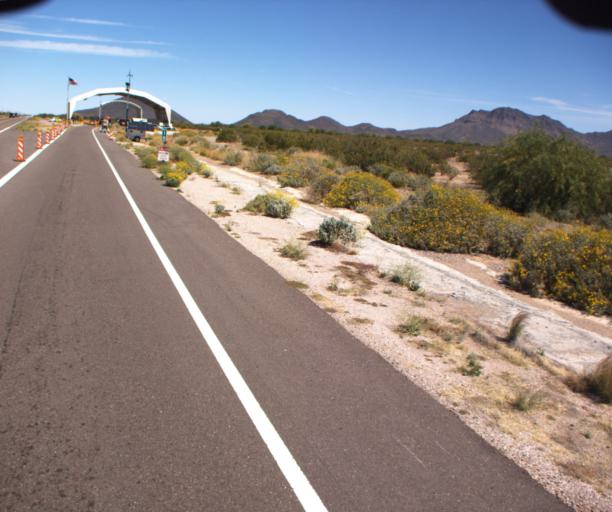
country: US
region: Arizona
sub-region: Maricopa County
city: Gila Bend
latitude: 32.7132
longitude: -112.8430
